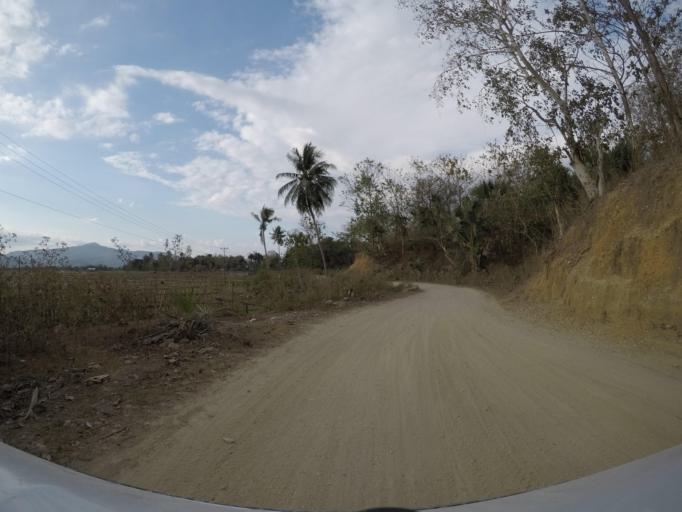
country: TL
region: Bobonaro
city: Maliana
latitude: -8.8866
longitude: 125.2084
